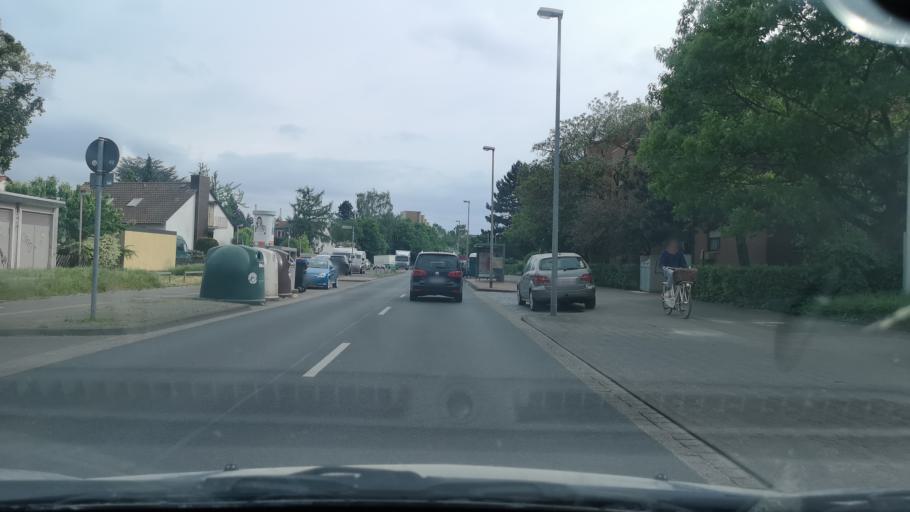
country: DE
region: Lower Saxony
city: Hannover
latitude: 52.4006
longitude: 9.6938
